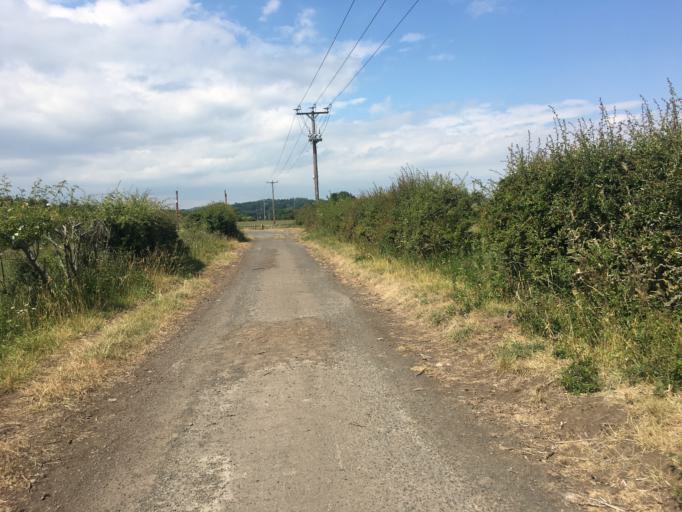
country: GB
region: England
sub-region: Northumberland
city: Belford
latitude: 55.5984
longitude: -1.7991
